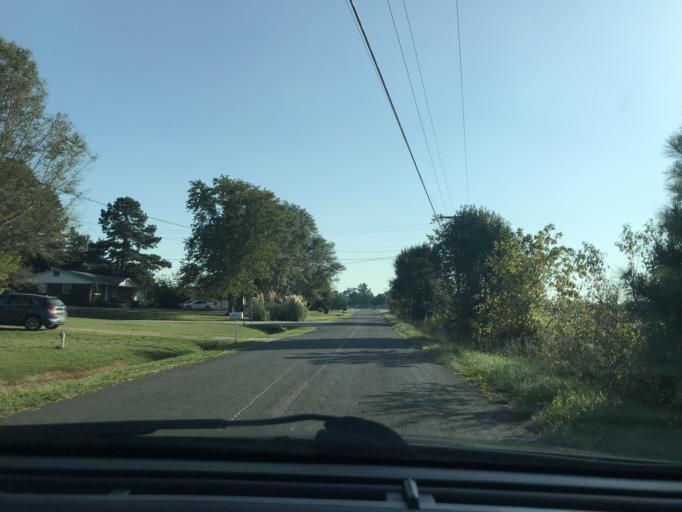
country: US
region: North Carolina
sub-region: Cleveland County
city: Boiling Springs
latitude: 35.1708
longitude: -81.7295
